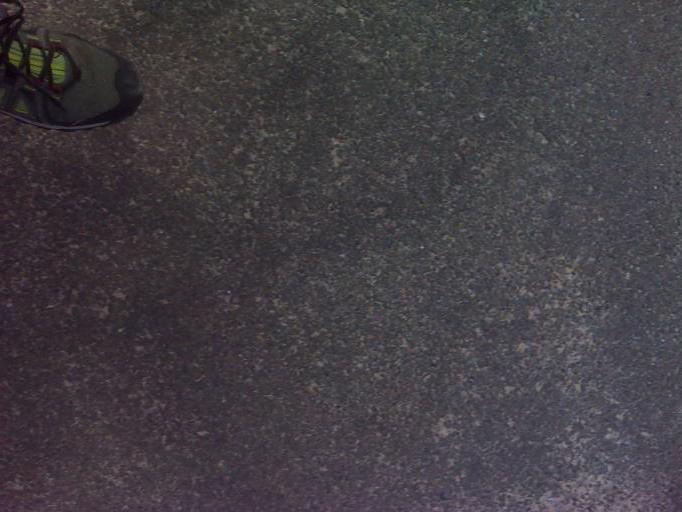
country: FR
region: Aquitaine
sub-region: Departement des Landes
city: Capbreton
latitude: 43.6670
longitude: -1.4397
